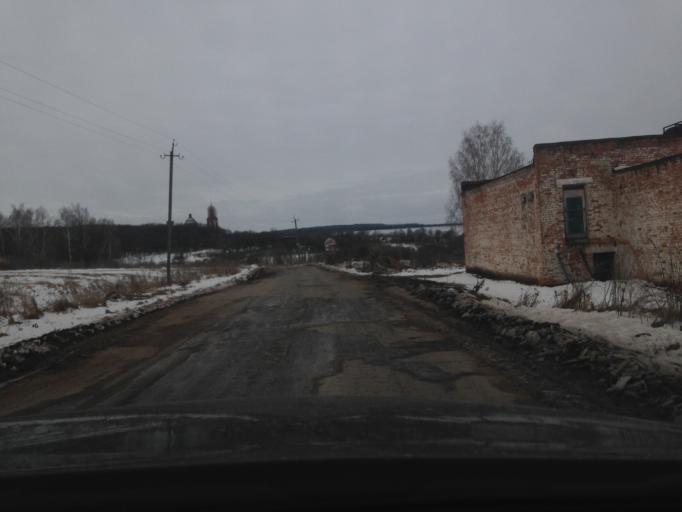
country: RU
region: Tula
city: Priupskiy
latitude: 53.7738
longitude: 37.6466
